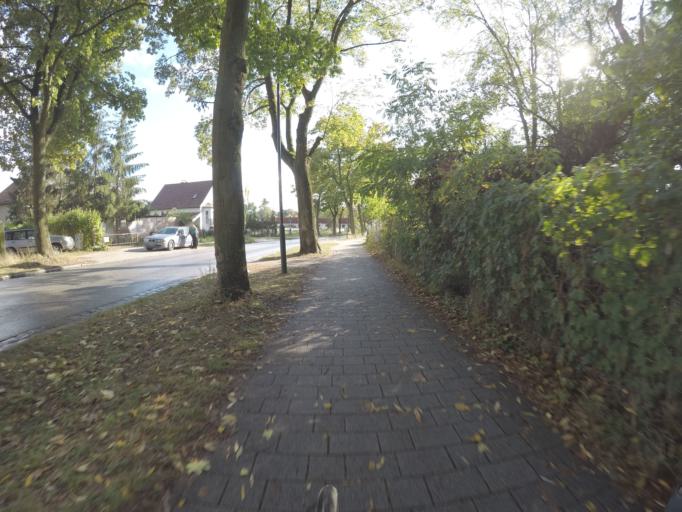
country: DE
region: Brandenburg
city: Petershagen
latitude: 52.5286
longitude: 13.7910
